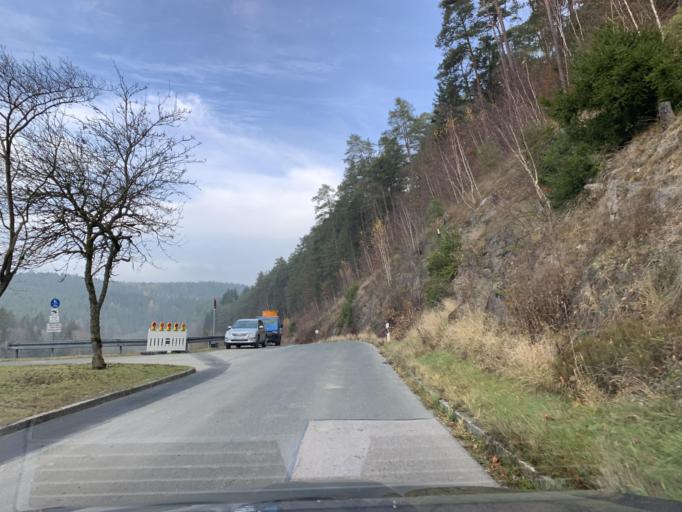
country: DE
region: Bavaria
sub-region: Upper Palatinate
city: Thanstein
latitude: 49.3570
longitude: 12.4489
